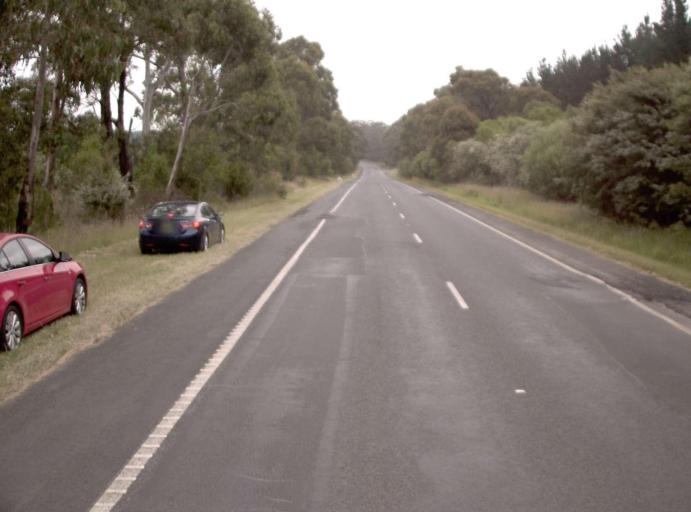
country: AU
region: Victoria
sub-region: Latrobe
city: Moe
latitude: -38.2978
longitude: 146.2854
